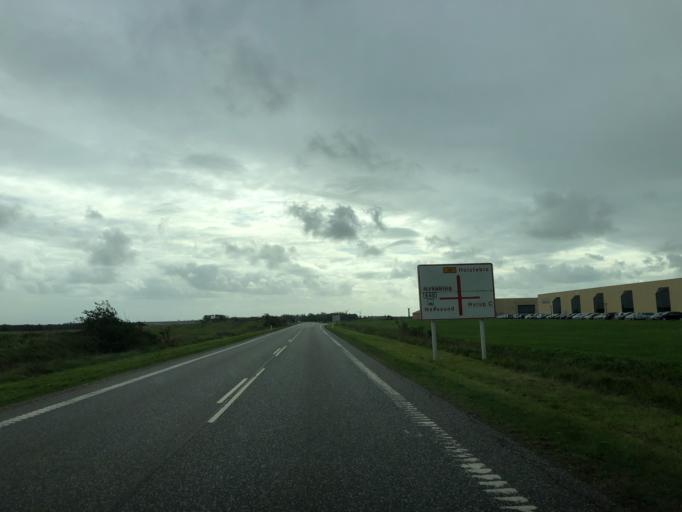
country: DK
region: North Denmark
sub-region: Thisted Kommune
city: Hurup
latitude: 56.7462
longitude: 8.4411
